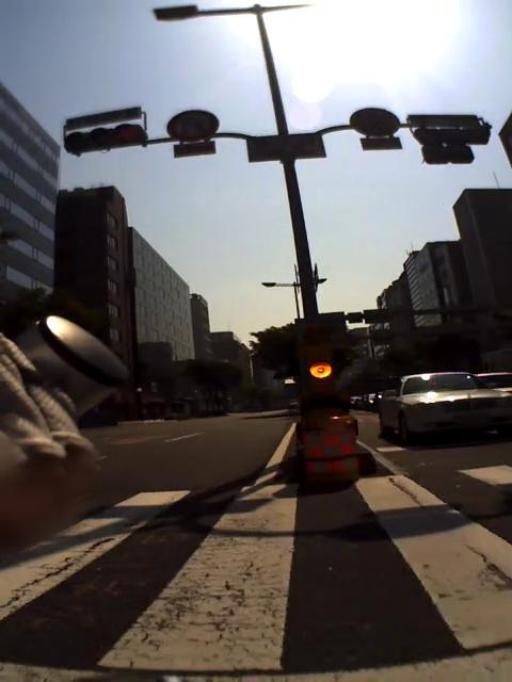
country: JP
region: Osaka
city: Osaka-shi
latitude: 34.6980
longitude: 135.5062
